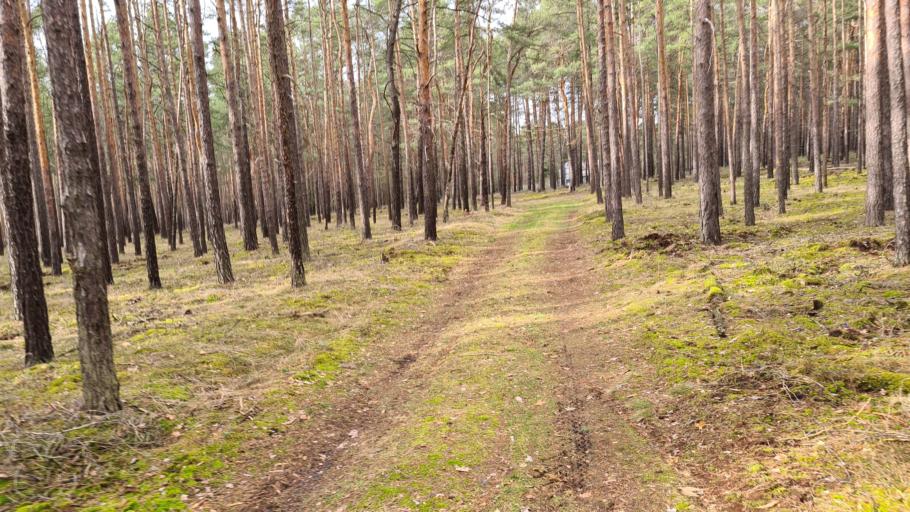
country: DE
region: Brandenburg
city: Schilda
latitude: 51.6125
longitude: 13.3998
